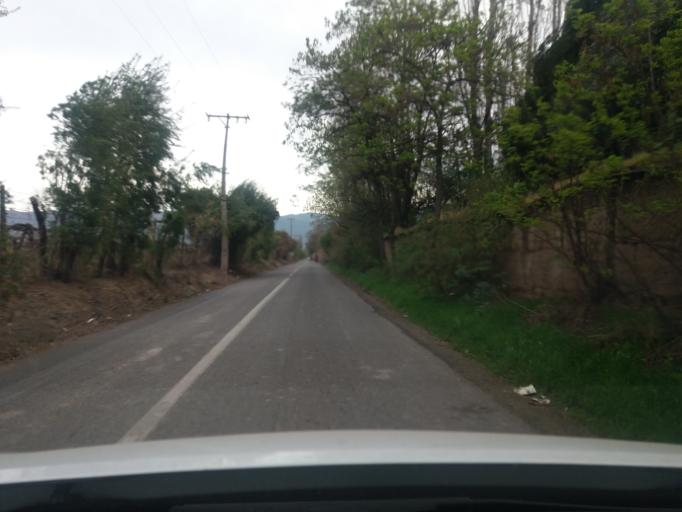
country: CL
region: Valparaiso
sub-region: Provincia de Los Andes
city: Los Andes
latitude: -32.8532
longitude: -70.6406
